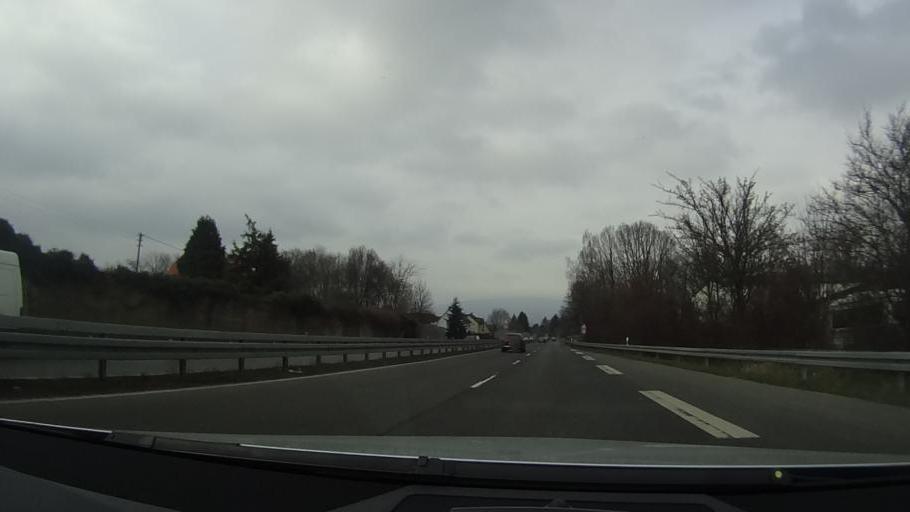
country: DE
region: Hesse
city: Schwalbach am Taunus
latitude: 50.1528
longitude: 8.5468
